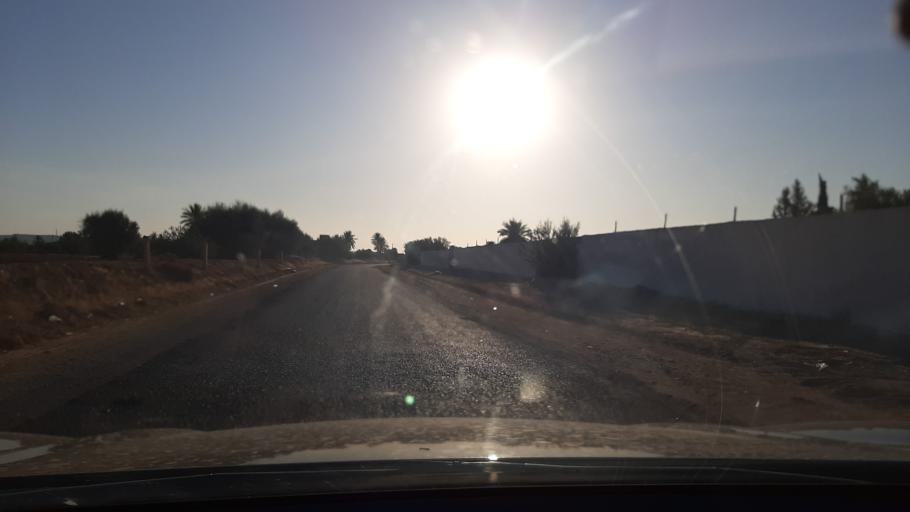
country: TN
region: Qabis
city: Matmata
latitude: 33.6175
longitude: 10.2601
